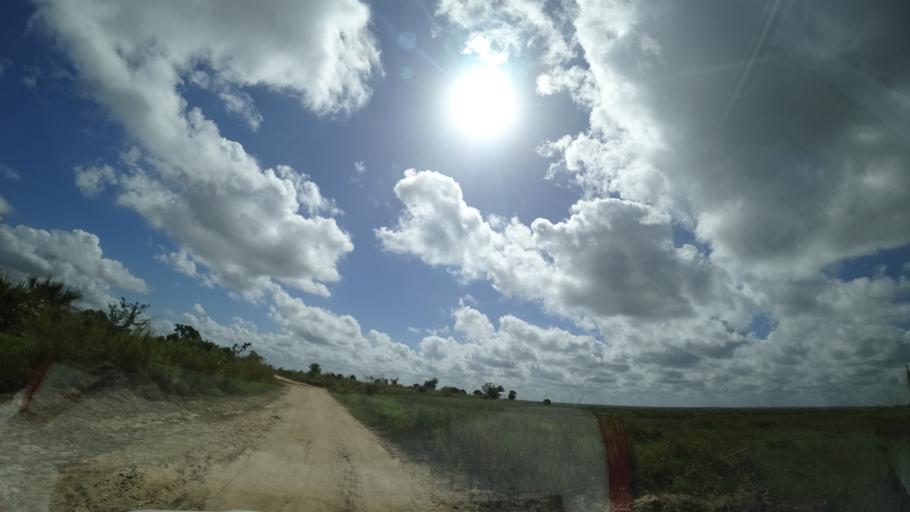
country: MZ
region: Sofala
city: Dondo
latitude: -19.4249
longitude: 34.5622
